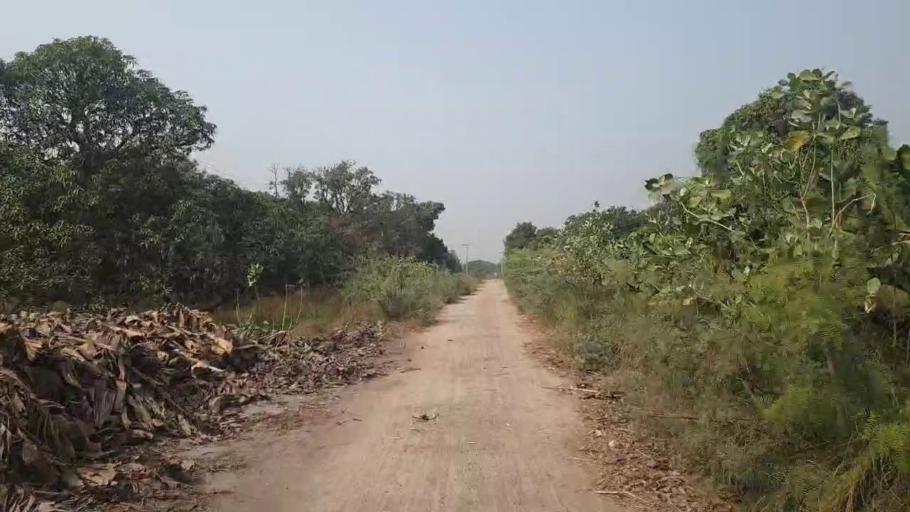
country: PK
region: Sindh
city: Tando Muhammad Khan
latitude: 25.2692
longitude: 68.5818
